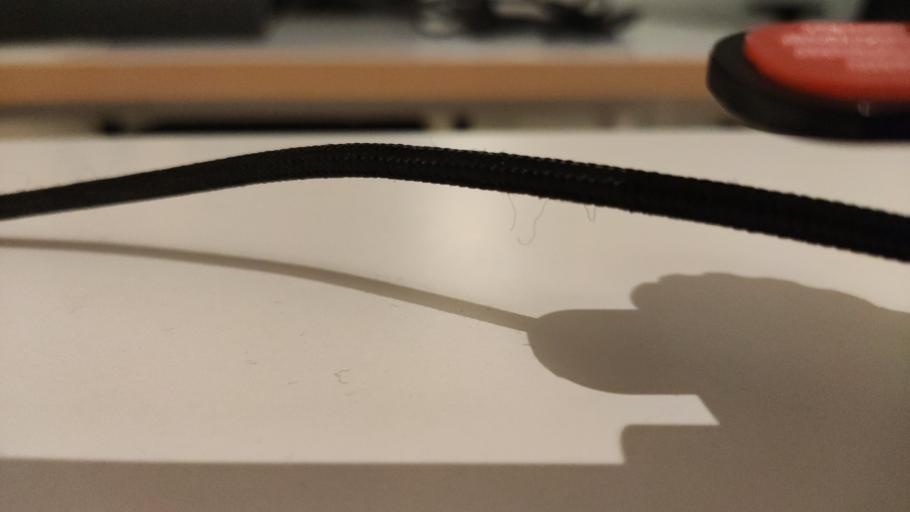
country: RU
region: Moskovskaya
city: Il'inskiy Pogost
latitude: 55.5312
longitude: 38.8725
